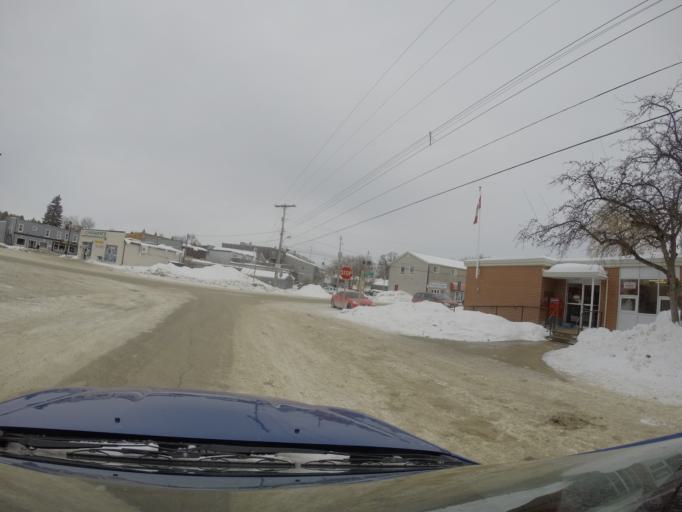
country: CA
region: Ontario
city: Wasaga Beach
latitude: 44.4189
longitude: -80.0903
